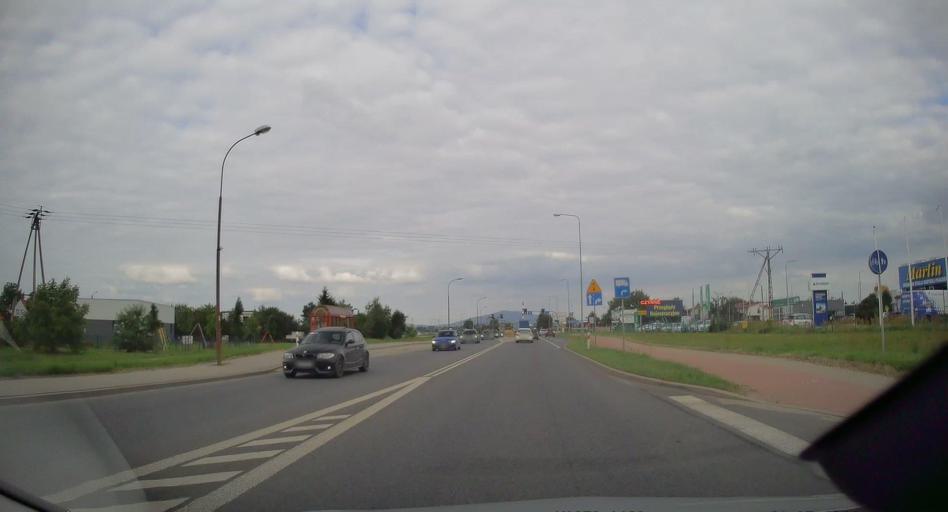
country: PL
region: Lower Silesian Voivodeship
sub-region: Powiat swidnicki
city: Swidnica
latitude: 50.8557
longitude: 16.5103
